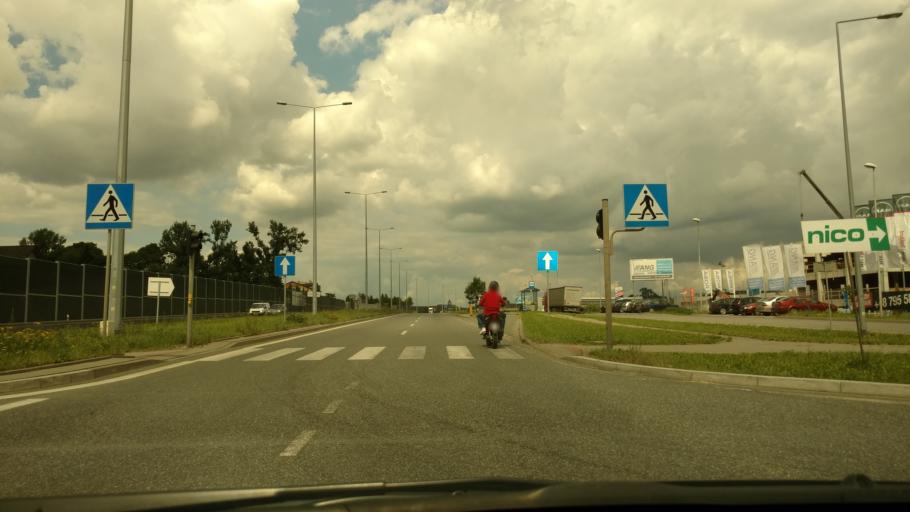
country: PL
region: Lesser Poland Voivodeship
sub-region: Powiat krakowski
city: Modlniczka
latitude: 50.1127
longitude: 19.8732
